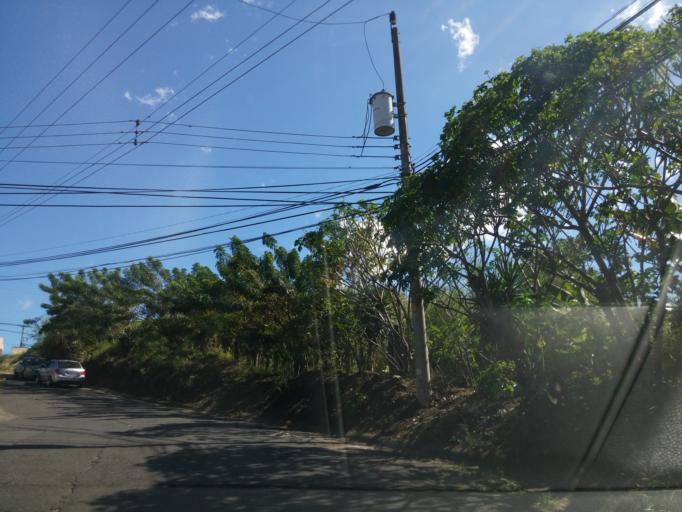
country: CR
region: San Jose
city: Colima
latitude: 9.9424
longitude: -84.0940
